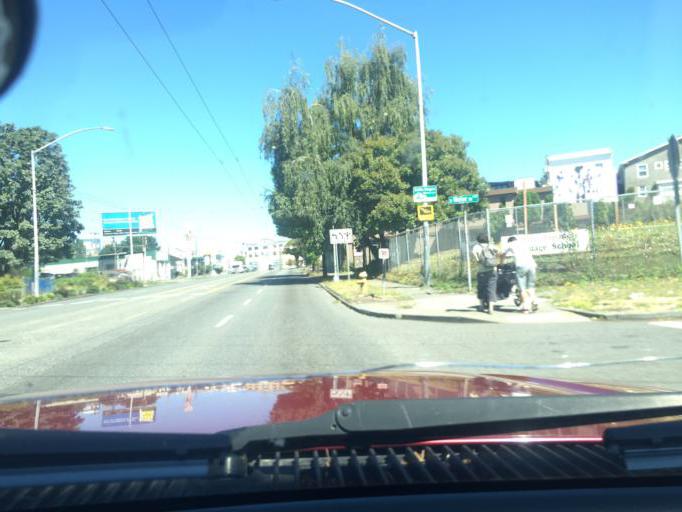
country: US
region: Washington
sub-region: King County
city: Seattle
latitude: 47.5973
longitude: -122.3126
